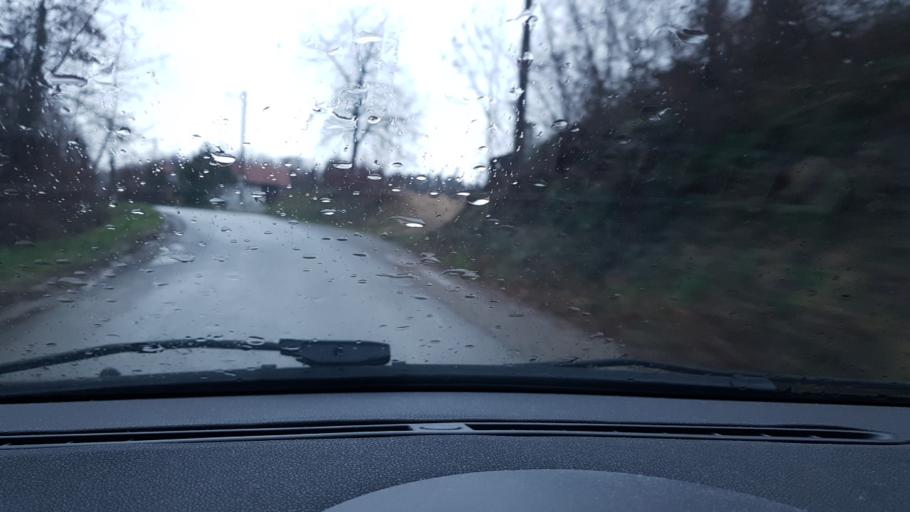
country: HR
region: Krapinsko-Zagorska
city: Bedekovcina
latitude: 45.9958
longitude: 15.9844
